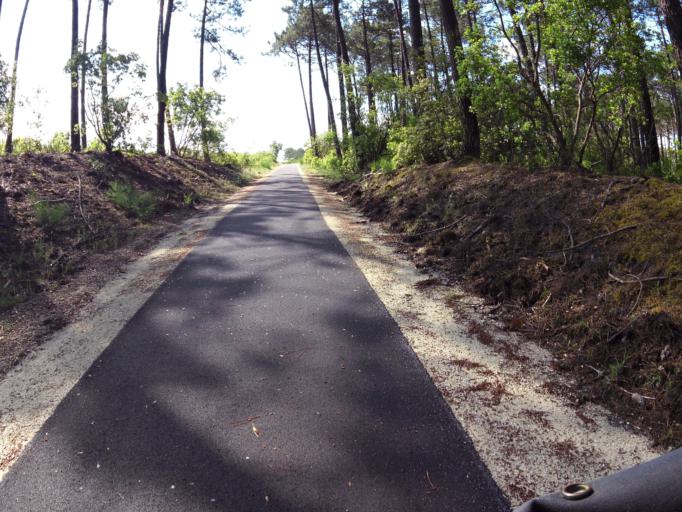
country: FR
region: Aquitaine
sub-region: Departement de la Gironde
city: Lacanau
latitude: 45.0339
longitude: -1.1806
